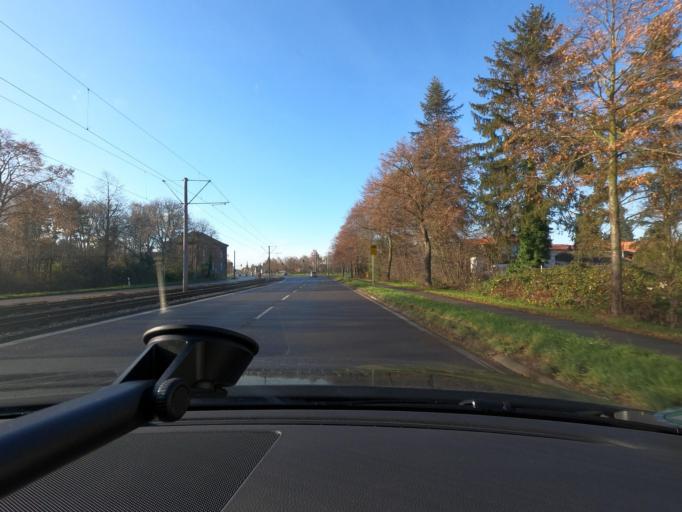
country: DE
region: North Rhine-Westphalia
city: Tonisvorst
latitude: 51.3249
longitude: 6.5178
